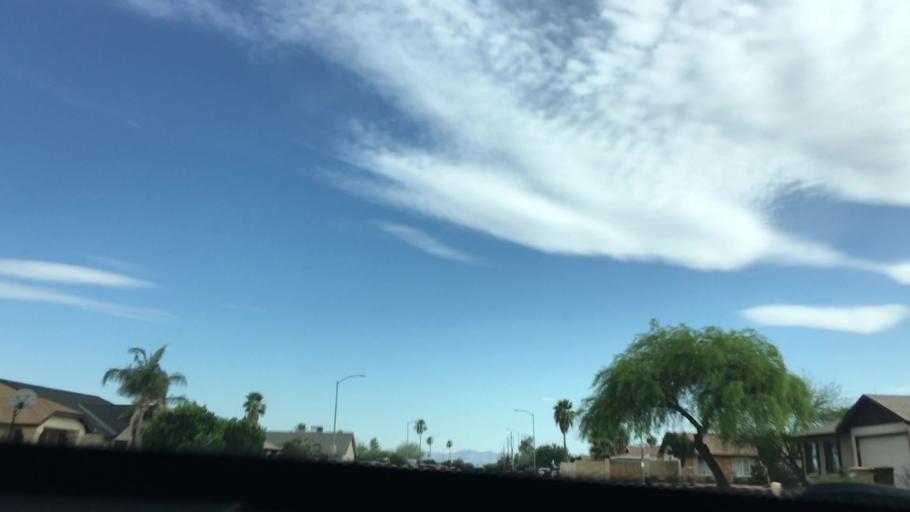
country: US
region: Arizona
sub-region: Maricopa County
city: Peoria
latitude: 33.5871
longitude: -112.2291
